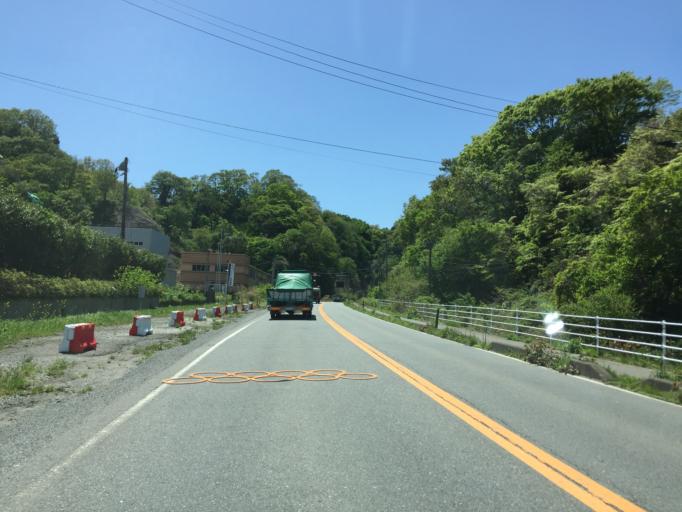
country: JP
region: Fukushima
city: Iwaki
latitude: 36.9625
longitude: 140.8718
